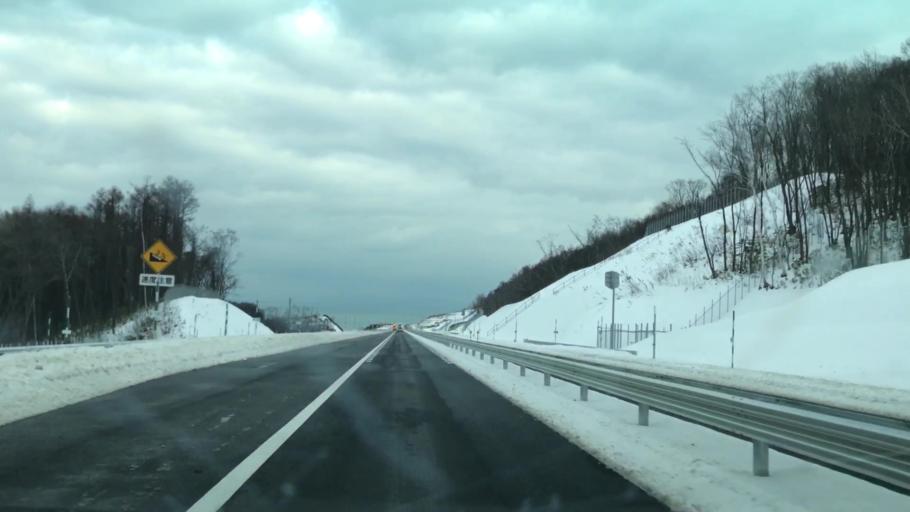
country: JP
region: Hokkaido
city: Otaru
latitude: 43.1637
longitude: 141.0589
